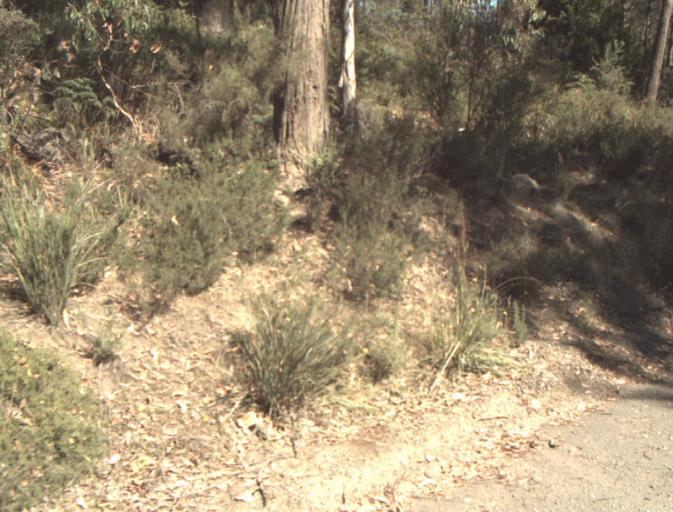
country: AU
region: Tasmania
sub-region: Launceston
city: Mayfield
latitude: -41.3383
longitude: 147.2084
